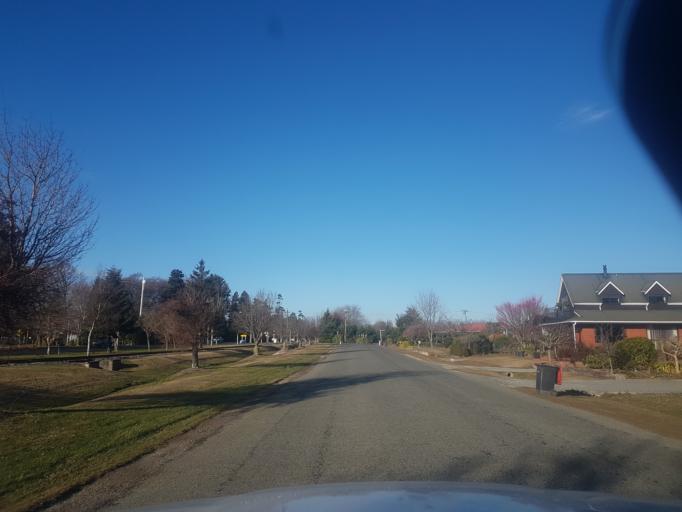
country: NZ
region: Canterbury
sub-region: Timaru District
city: Pleasant Point
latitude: -44.2642
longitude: 171.1402
